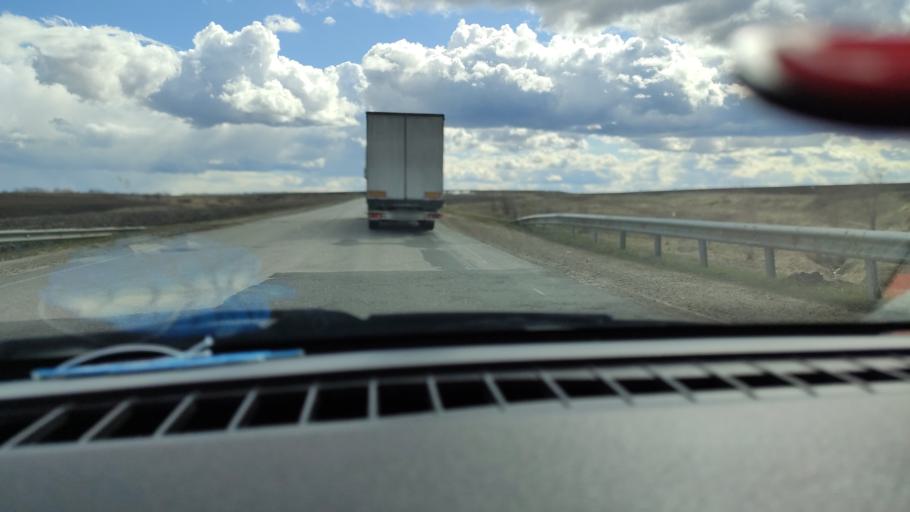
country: RU
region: Samara
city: Syzran'
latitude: 53.0080
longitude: 48.3322
